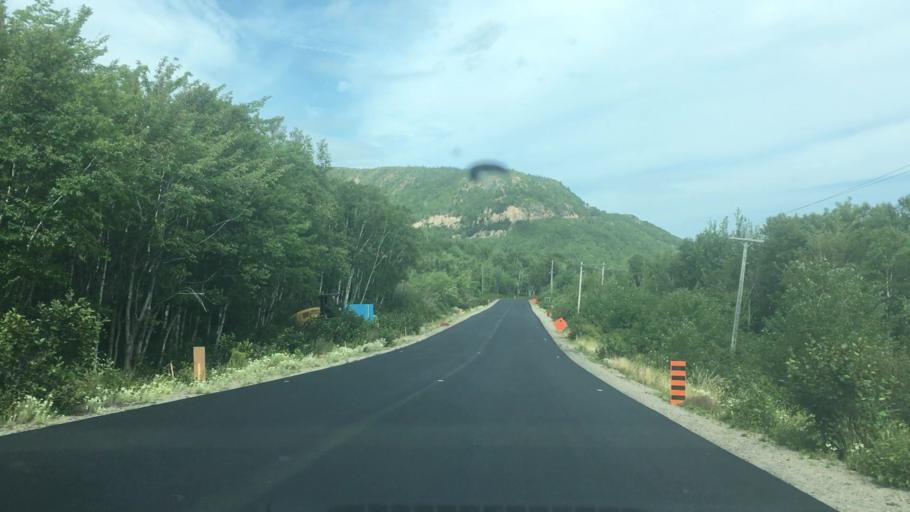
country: CA
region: Nova Scotia
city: Sydney Mines
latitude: 46.5732
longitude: -60.3924
